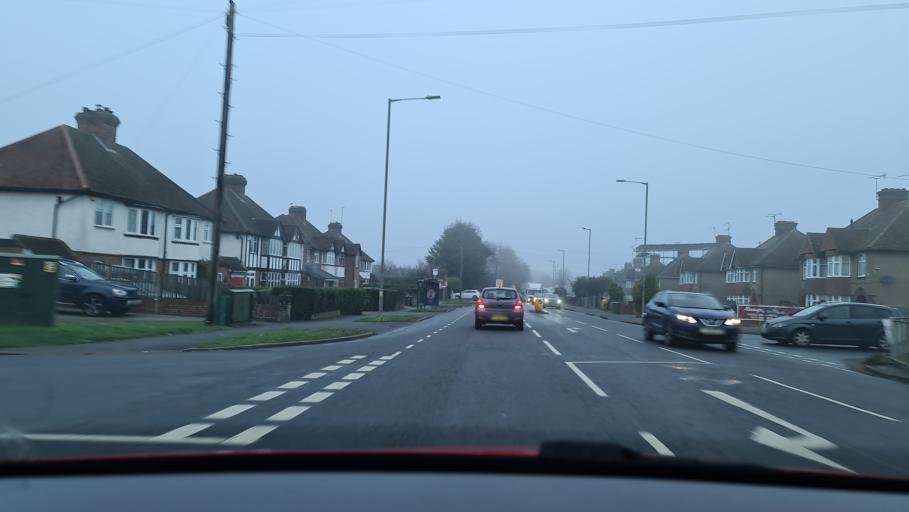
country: GB
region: England
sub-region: Buckinghamshire
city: Aylesbury
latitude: 51.8135
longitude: -0.7844
